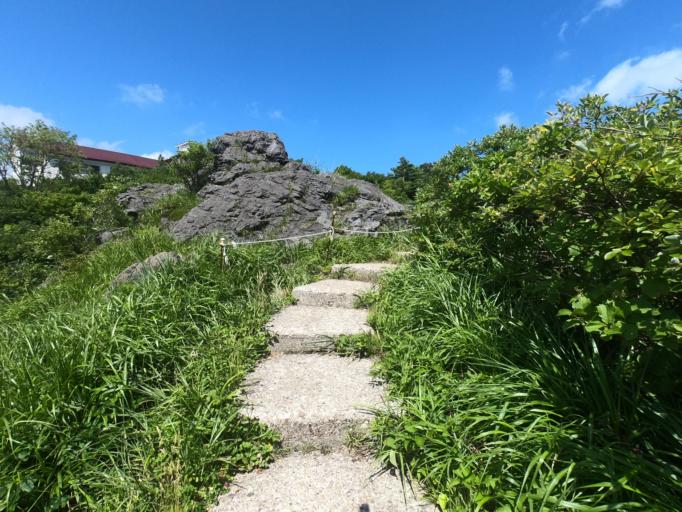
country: JP
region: Akita
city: Yuzawa
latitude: 38.9792
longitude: 140.7713
